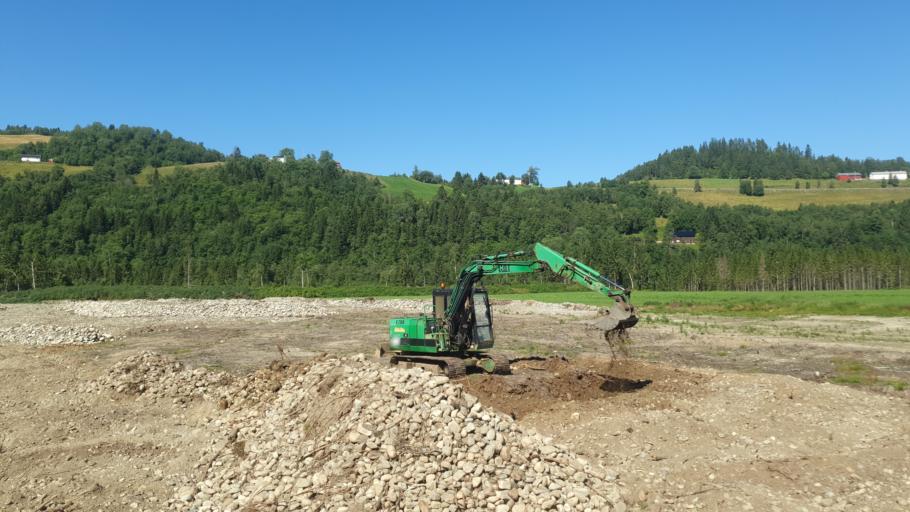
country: NO
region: Sor-Trondelag
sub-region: Meldal
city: Meldal
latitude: 63.1765
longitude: 9.7542
